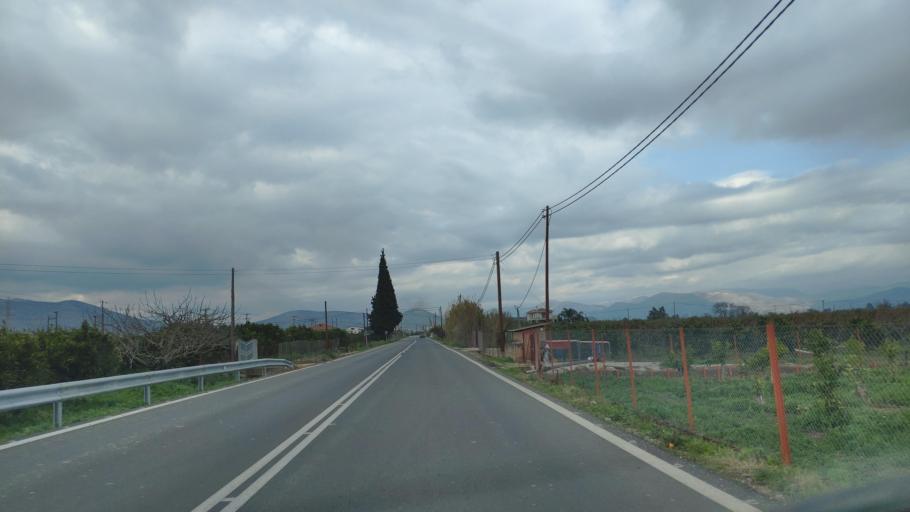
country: GR
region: Peloponnese
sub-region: Nomos Argolidos
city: Nea Kios
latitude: 37.5729
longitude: 22.7082
